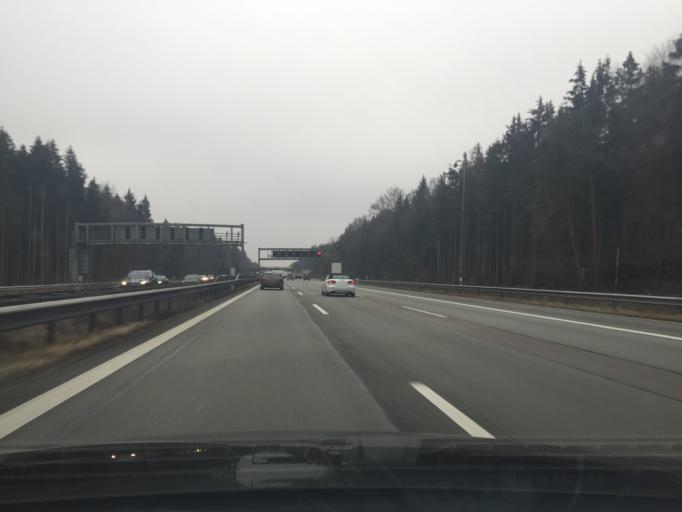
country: DE
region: Bavaria
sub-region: Upper Bavaria
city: Otterfing
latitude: 47.9352
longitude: 11.7055
